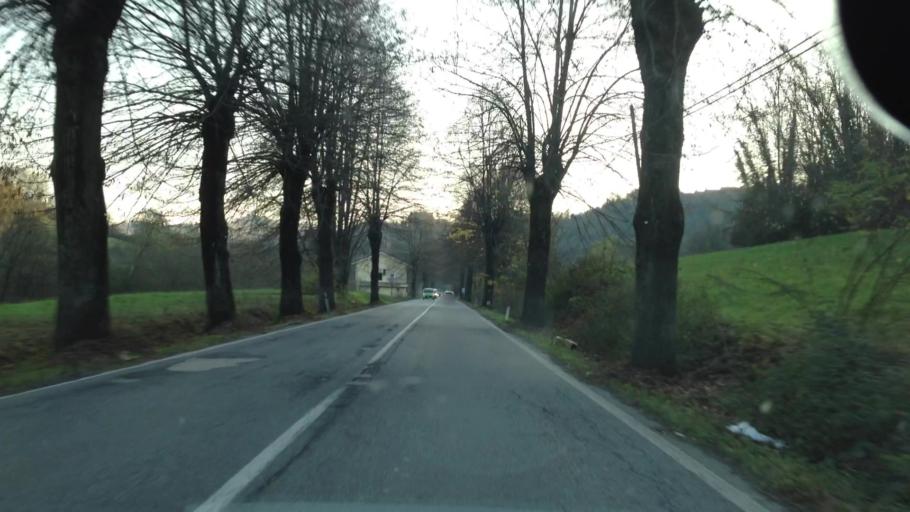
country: IT
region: Piedmont
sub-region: Provincia di Torino
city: Cavagnolo
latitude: 45.1402
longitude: 8.0554
